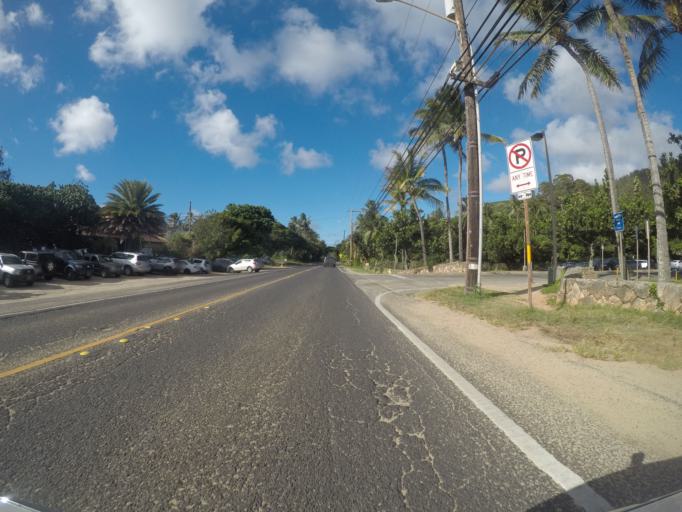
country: US
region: Hawaii
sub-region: Honolulu County
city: Pupukea
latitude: 21.6745
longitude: -158.0396
